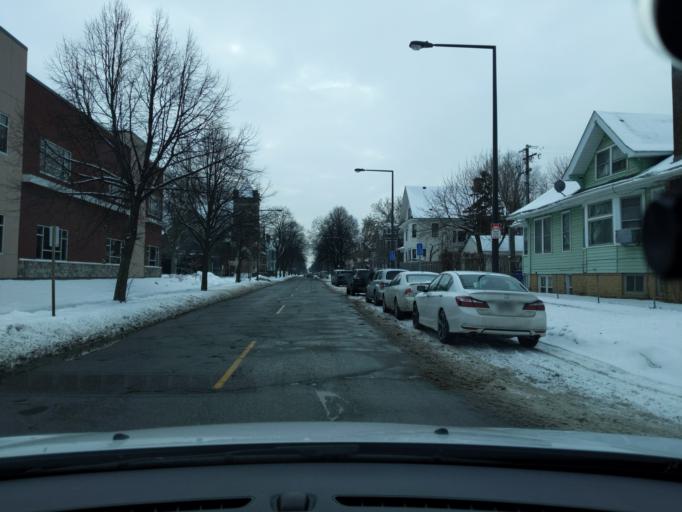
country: US
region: Minnesota
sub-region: Ramsey County
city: Saint Paul
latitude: 44.9458
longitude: -93.1365
